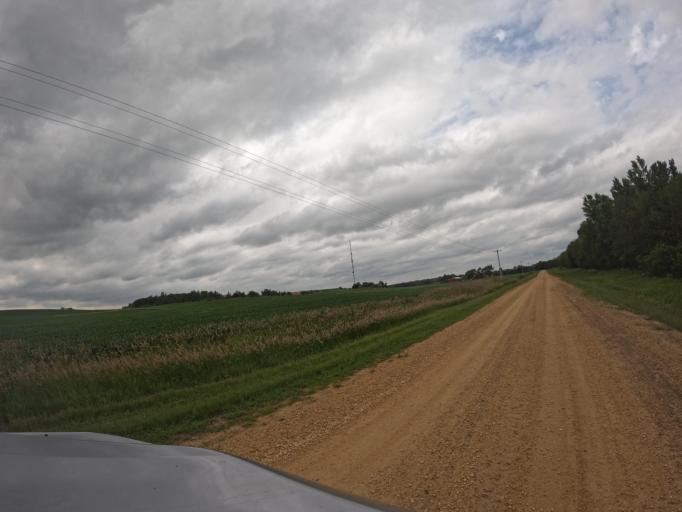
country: US
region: Iowa
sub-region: Clinton County
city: De Witt
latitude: 41.7995
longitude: -90.5683
